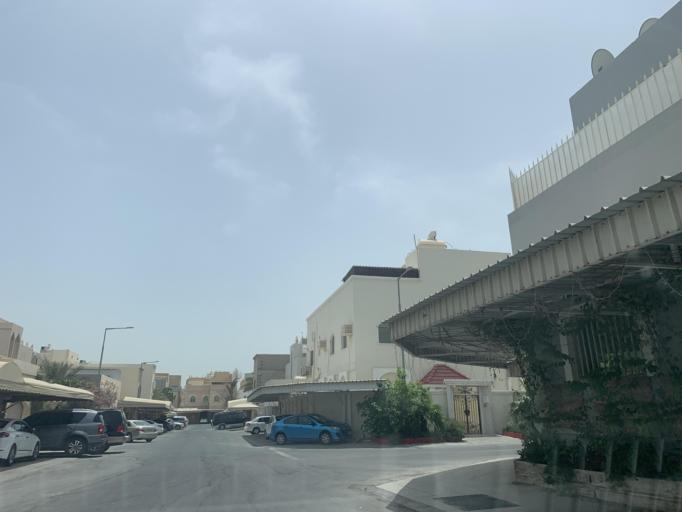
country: BH
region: Northern
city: Ar Rifa'
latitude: 26.1318
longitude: 50.5753
